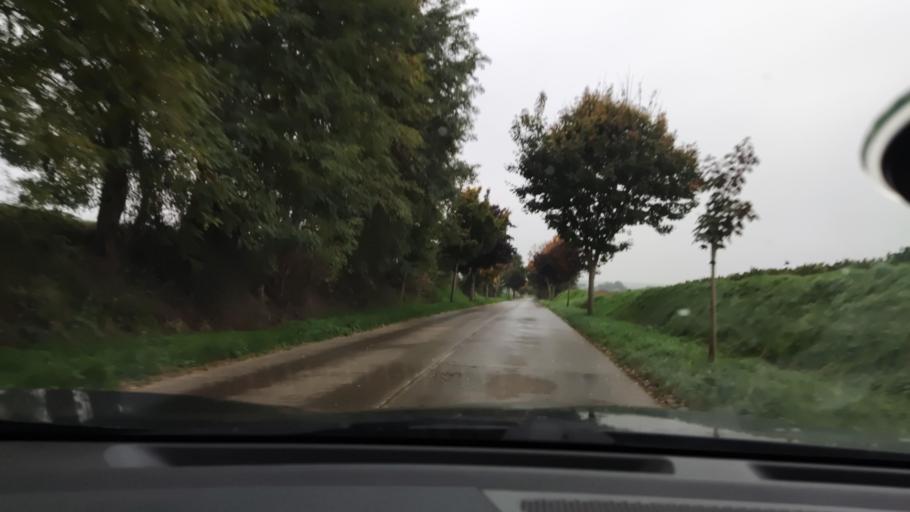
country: BE
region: Wallonia
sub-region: Province du Brabant Wallon
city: Jodoigne
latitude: 50.7320
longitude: 4.9085
